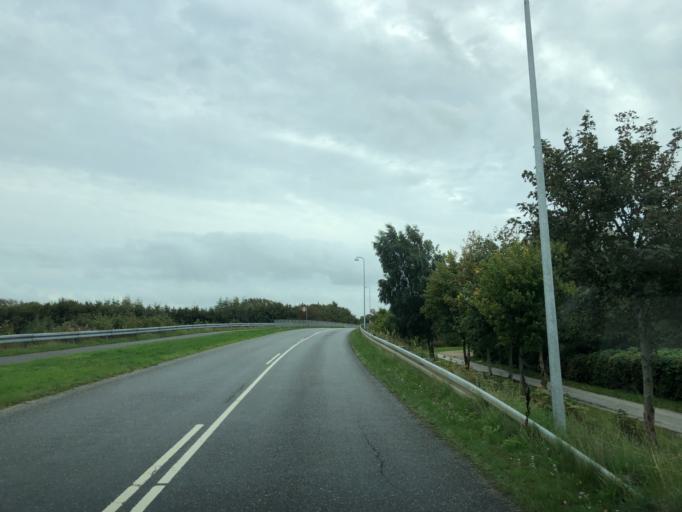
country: DK
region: Central Jutland
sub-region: Herning Kommune
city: Vildbjerg
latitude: 56.1812
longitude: 8.7447
